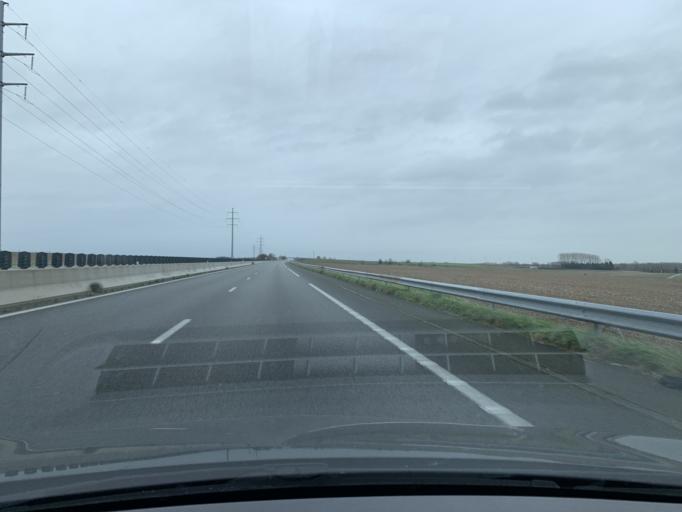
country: FR
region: Nord-Pas-de-Calais
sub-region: Departement du Nord
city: Escaudoeuvres
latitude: 50.2219
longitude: 3.2518
